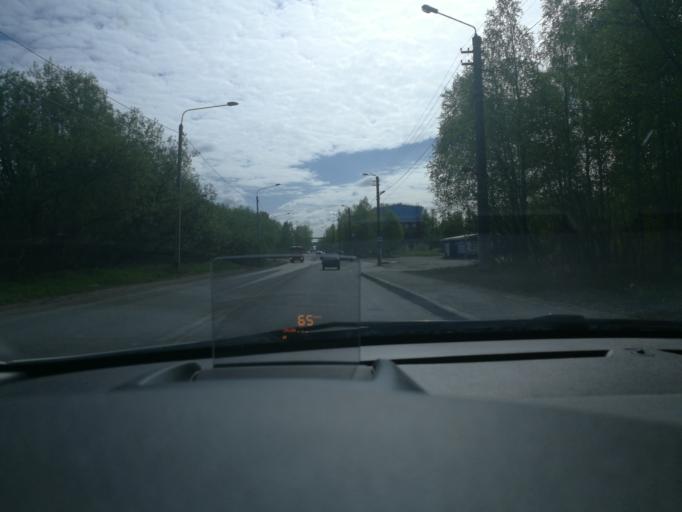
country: RU
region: Arkhangelskaya
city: Arkhangel'sk
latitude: 64.5972
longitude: 40.5631
